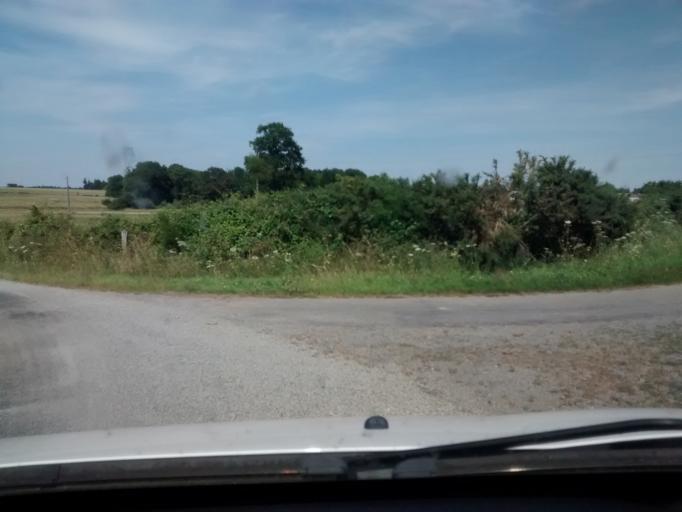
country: FR
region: Brittany
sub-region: Departement d'Ille-et-Vilaine
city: Acigne
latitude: 48.1047
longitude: -1.5602
